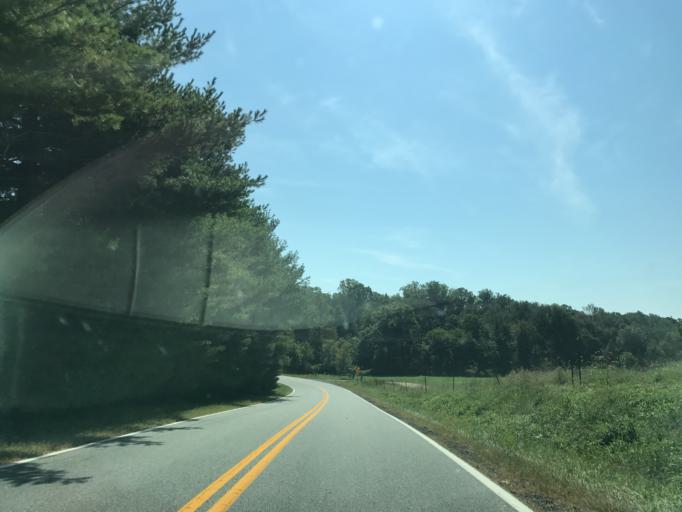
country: US
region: Maryland
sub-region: Queen Anne's County
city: Kingstown
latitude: 39.3072
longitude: -75.9686
